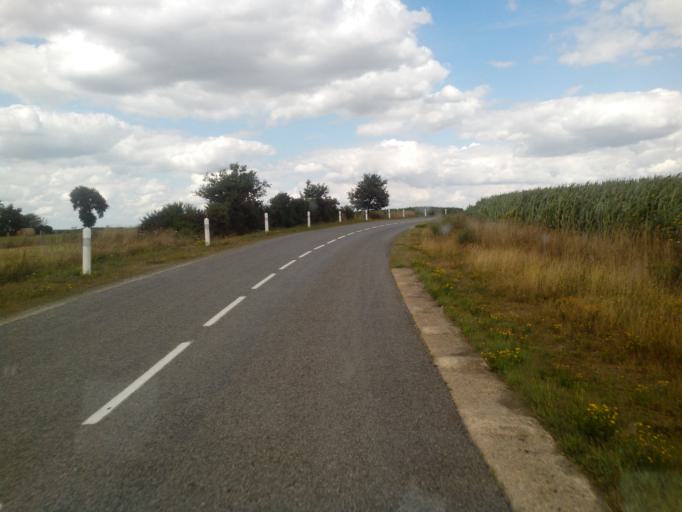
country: FR
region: Brittany
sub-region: Departement du Morbihan
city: Josselin
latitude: 48.0024
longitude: -2.5064
